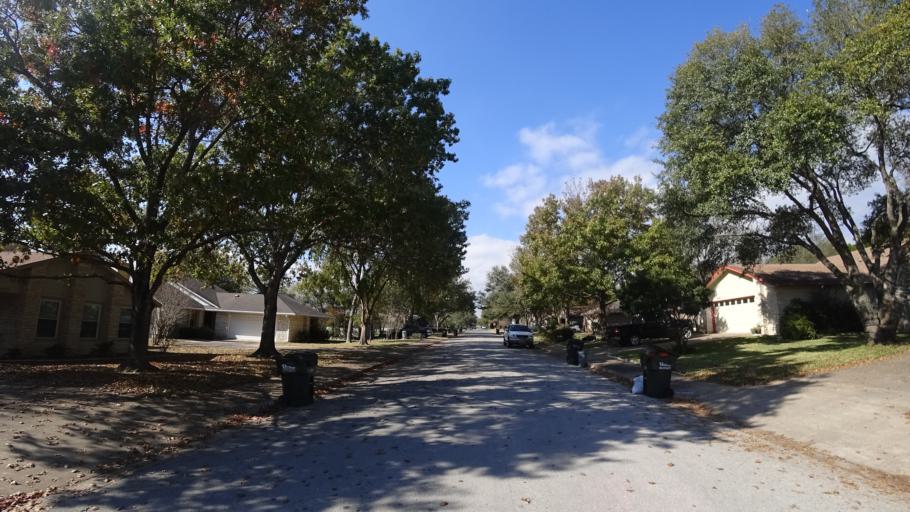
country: US
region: Texas
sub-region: Travis County
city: Shady Hollow
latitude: 30.1727
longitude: -97.8651
